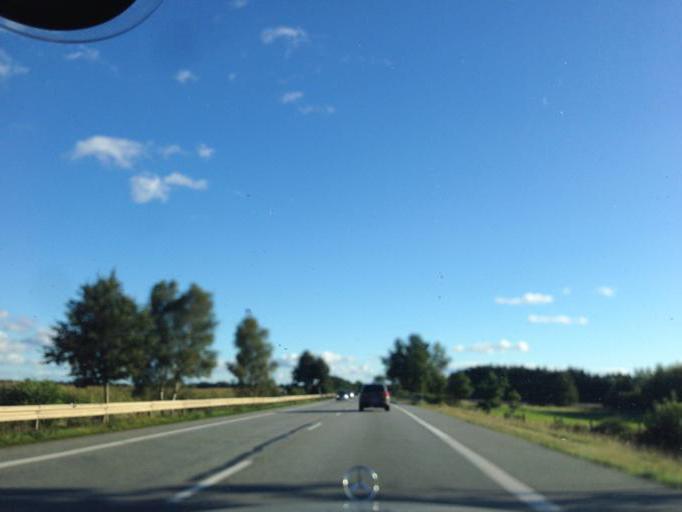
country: DE
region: Schleswig-Holstein
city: Rickling
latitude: 53.9952
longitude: 10.1828
